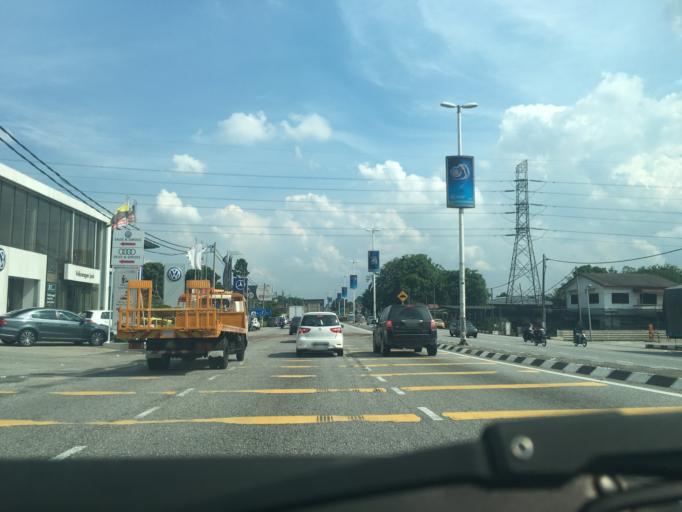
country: MY
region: Perak
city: Ipoh
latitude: 4.6243
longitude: 101.0815
